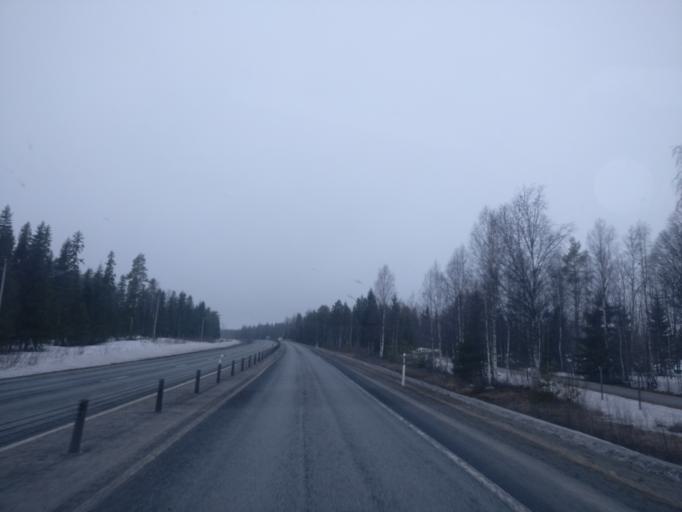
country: FI
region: Lapland
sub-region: Kemi-Tornio
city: Simo
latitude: 65.6683
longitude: 24.9668
